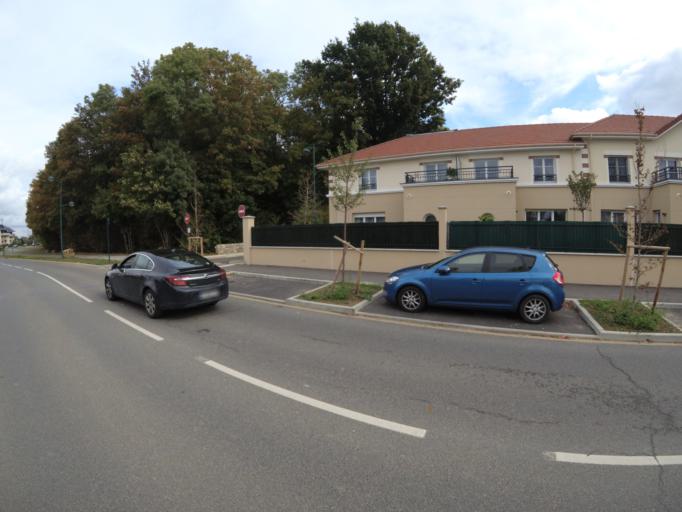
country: FR
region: Ile-de-France
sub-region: Departement de Seine-et-Marne
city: Montevrain
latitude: 48.8675
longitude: 2.7615
